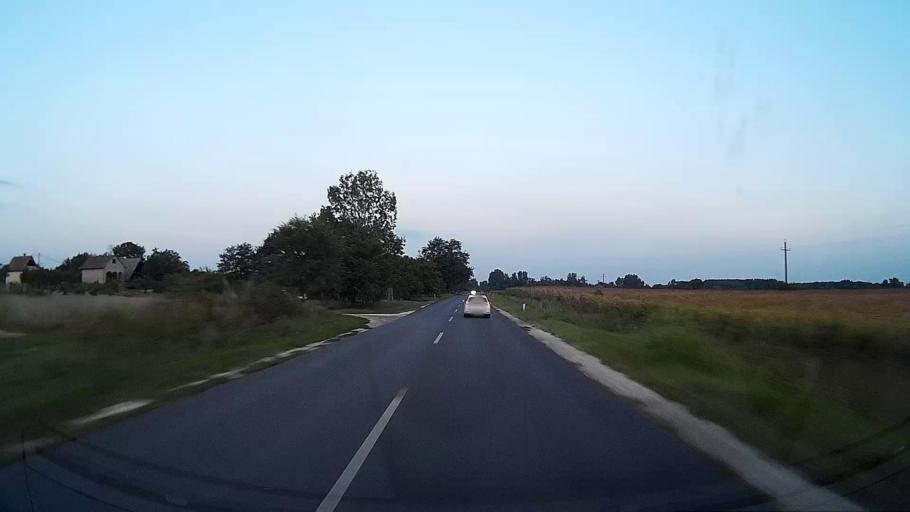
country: HU
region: Pest
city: Albertirsa
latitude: 47.2437
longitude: 19.6340
